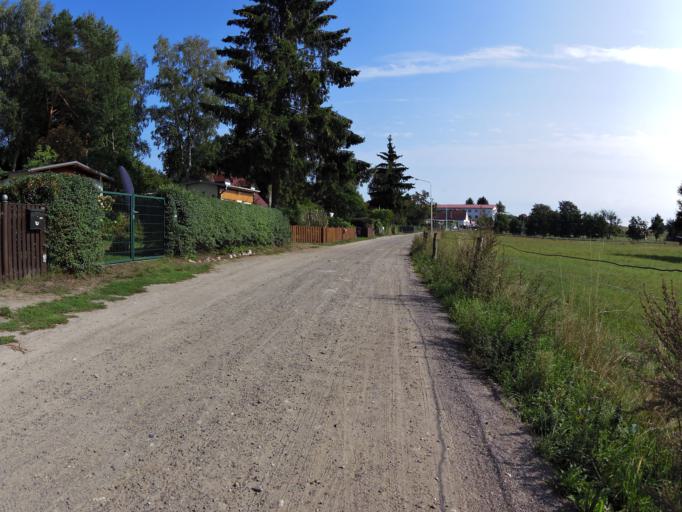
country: DE
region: Mecklenburg-Vorpommern
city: Seebad Bansin
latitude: 53.9584
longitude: 14.1415
